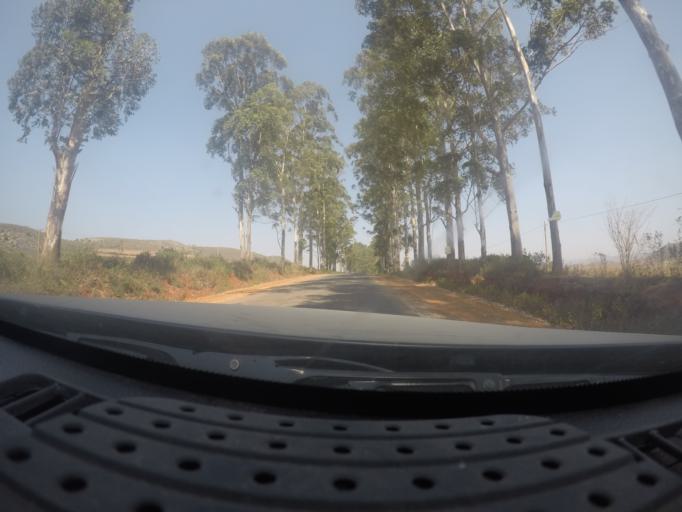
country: MM
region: Shan
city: Taunggyi
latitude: 20.8438
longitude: 96.5962
